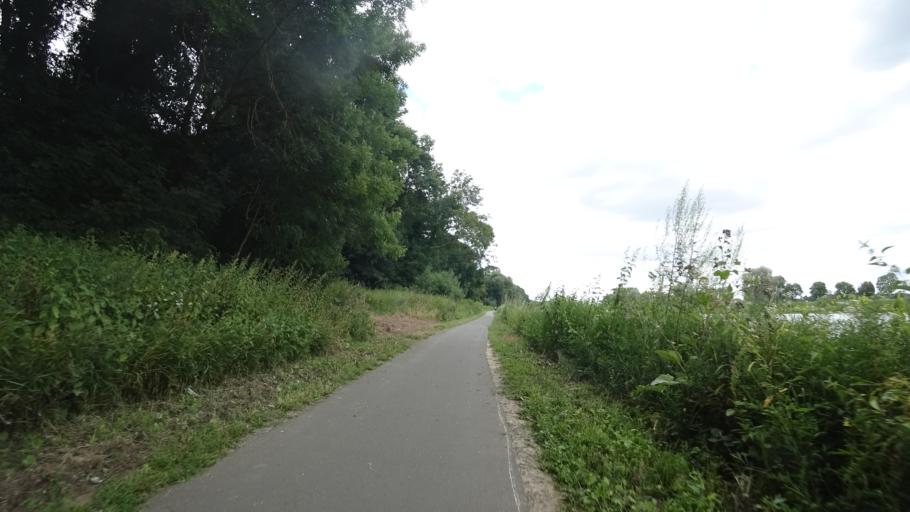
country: DE
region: North Rhine-Westphalia
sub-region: Regierungsbezirk Detmold
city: Minden
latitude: 52.3207
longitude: 8.9223
